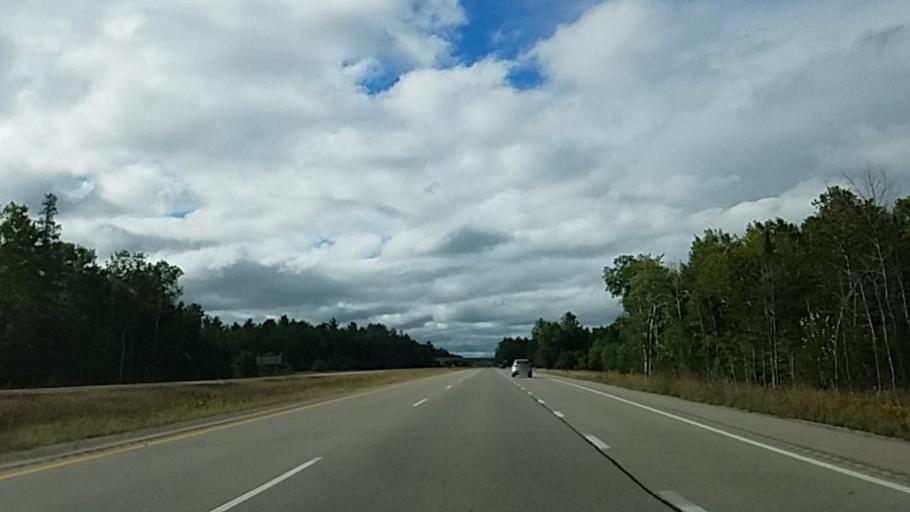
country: US
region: Michigan
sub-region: Mackinac County
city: Saint Ignace
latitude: 45.7385
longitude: -84.7288
